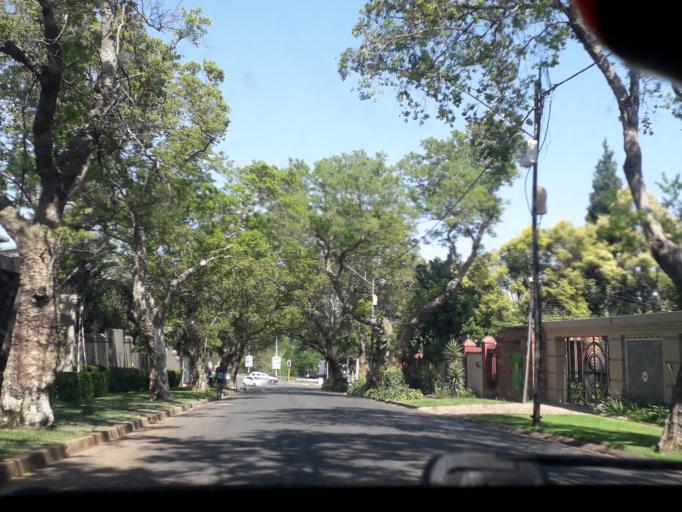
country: ZA
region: Gauteng
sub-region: City of Johannesburg Metropolitan Municipality
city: Johannesburg
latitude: -26.1479
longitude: 28.0598
